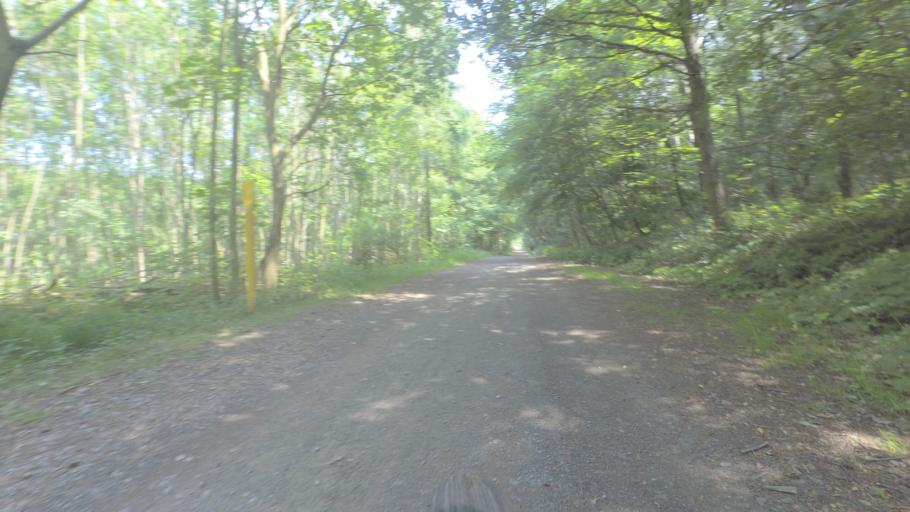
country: DE
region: Saxony-Anhalt
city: Rieder
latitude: 51.7257
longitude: 11.1636
